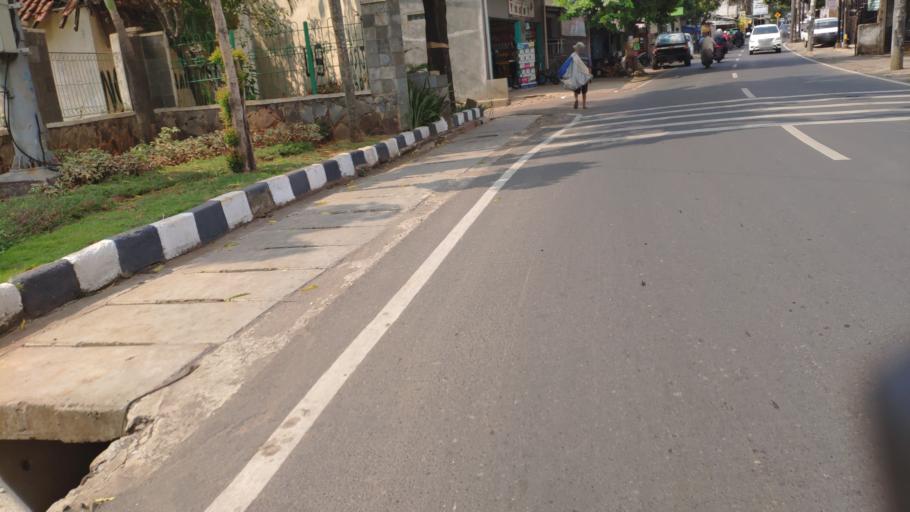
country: ID
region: West Java
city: Pamulang
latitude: -6.3197
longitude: 106.8107
